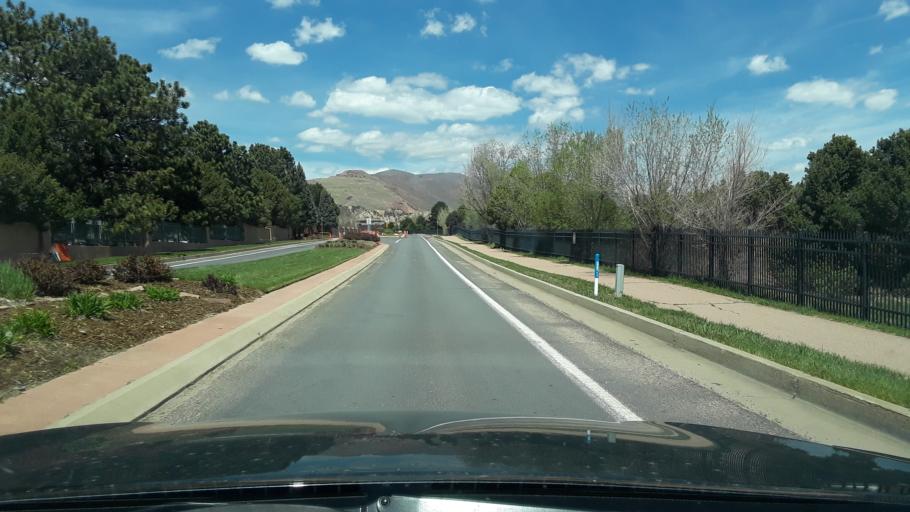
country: US
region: Colorado
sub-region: El Paso County
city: Manitou Springs
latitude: 38.8798
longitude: -104.8675
